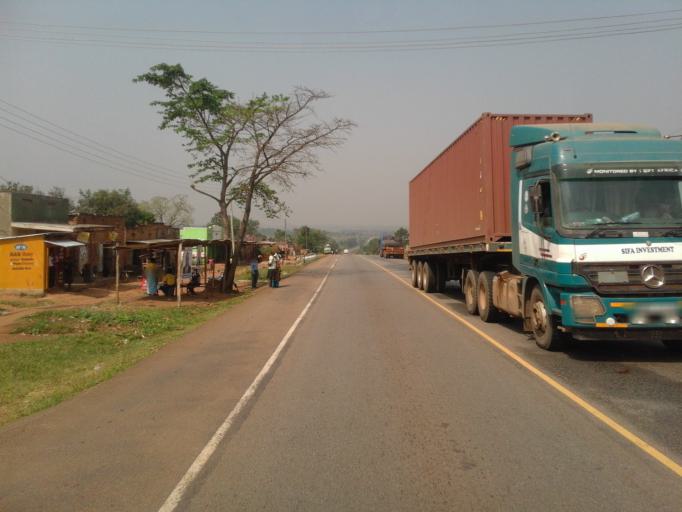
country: UG
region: Eastern Region
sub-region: Iganga District
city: Iganga
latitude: 0.6315
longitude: 33.5734
